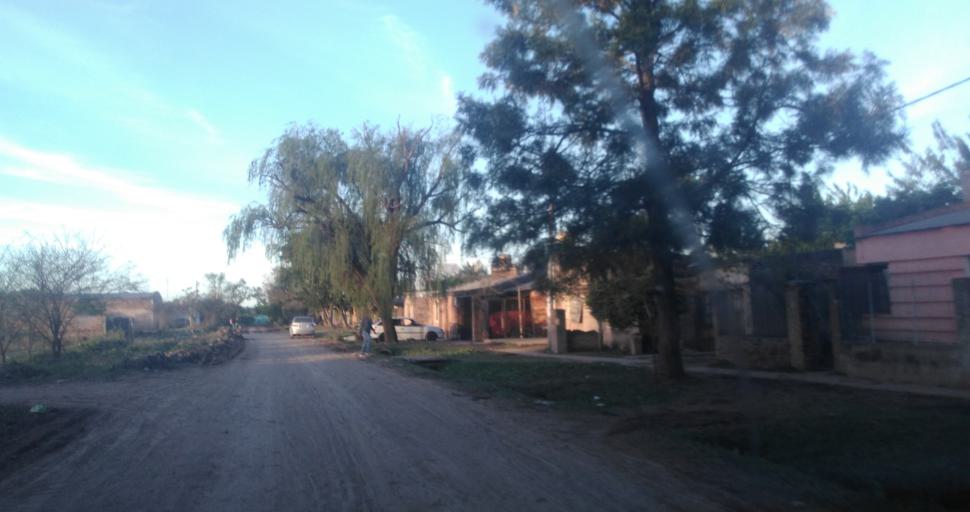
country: AR
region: Chaco
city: Fontana
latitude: -27.4273
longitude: -58.9968
